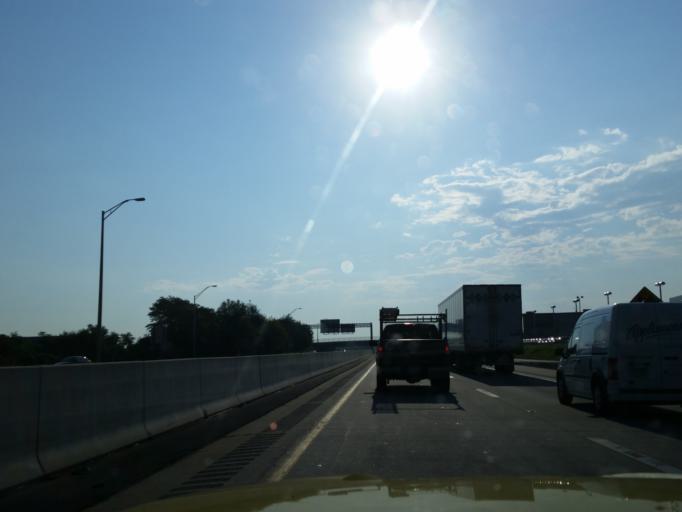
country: US
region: Pennsylvania
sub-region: Lancaster County
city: East Petersburg
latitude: 40.0608
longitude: -76.3586
